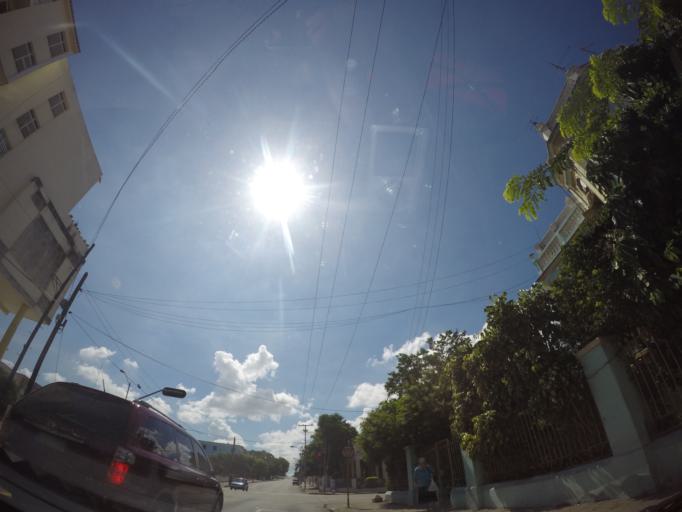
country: CU
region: La Habana
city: Regla
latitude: 23.0971
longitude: -82.3176
